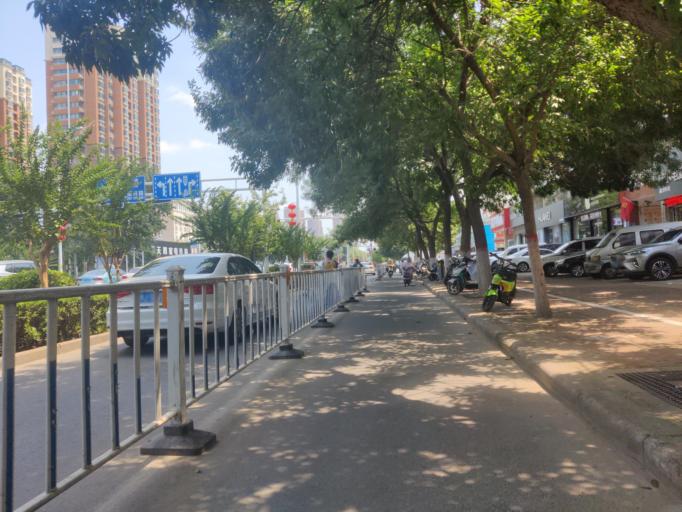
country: CN
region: Henan Sheng
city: Puyang
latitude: 35.7721
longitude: 115.0251
